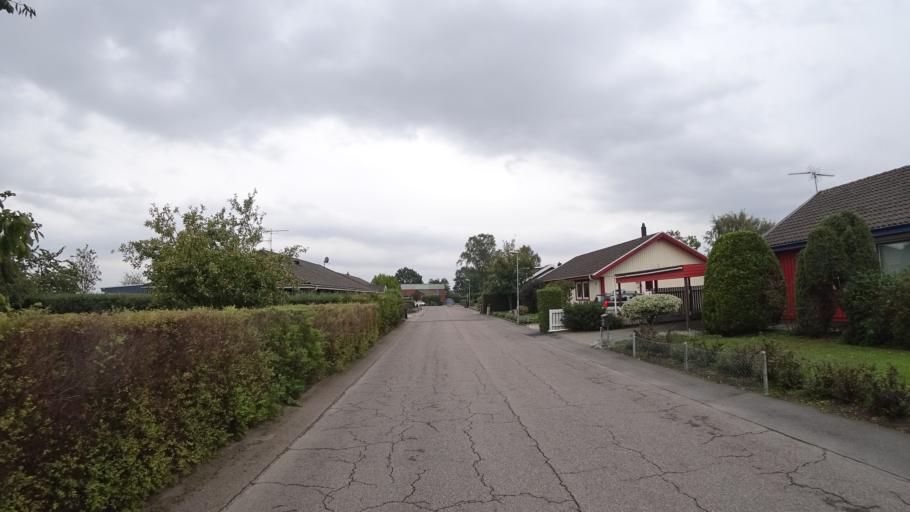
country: SE
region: Skane
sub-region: Kavlinge Kommun
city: Kaevlinge
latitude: 55.8063
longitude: 13.1155
